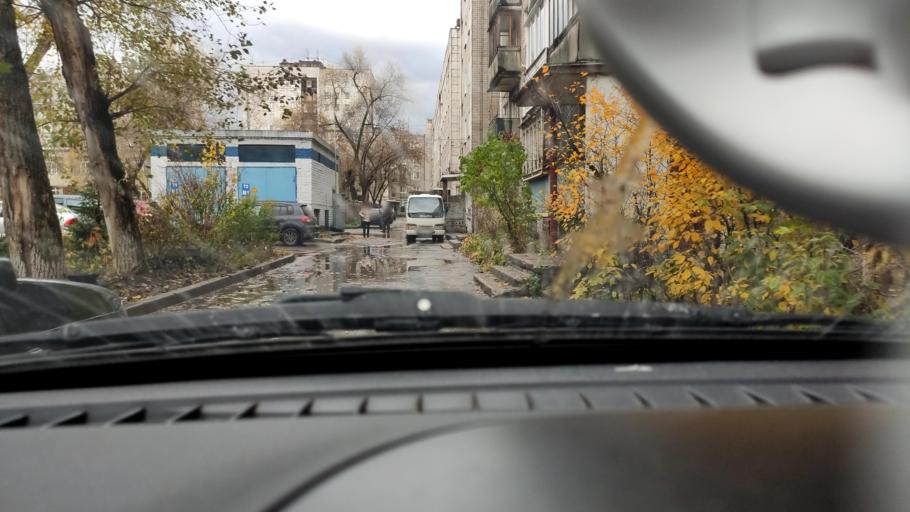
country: RU
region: Perm
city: Perm
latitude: 58.0109
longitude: 56.2109
